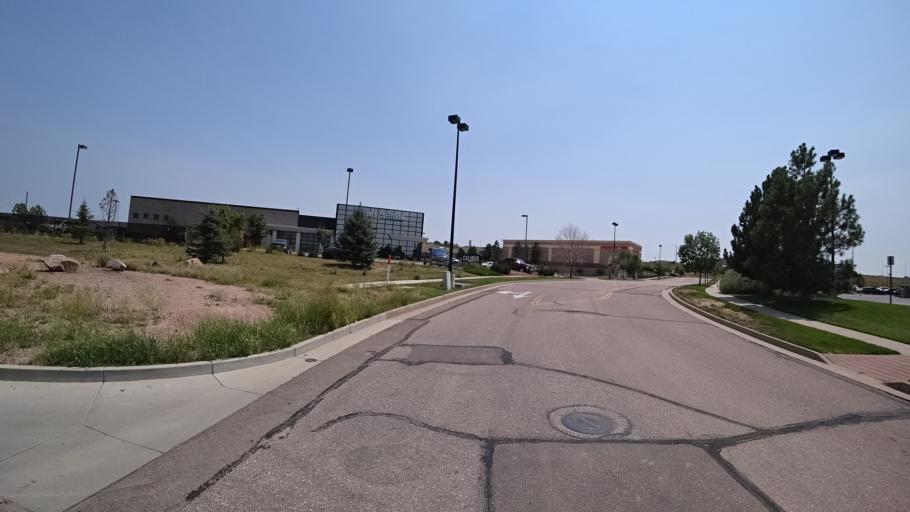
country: US
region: Colorado
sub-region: El Paso County
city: Black Forest
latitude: 38.9447
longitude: -104.7224
